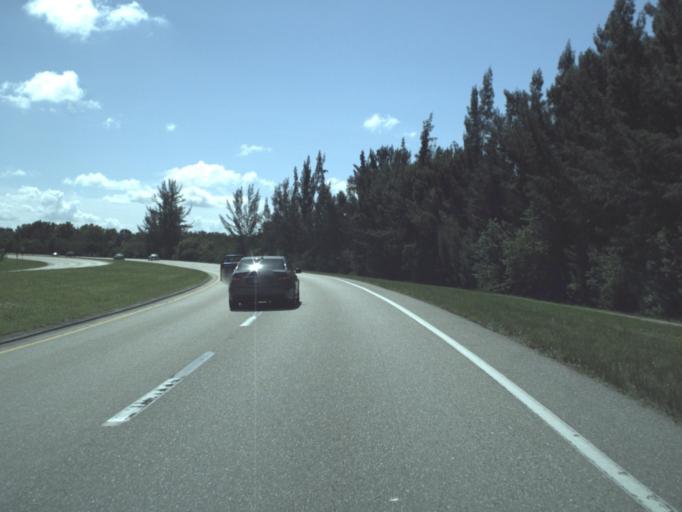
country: US
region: Florida
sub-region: Lee County
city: Pine Island Center
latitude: 26.6102
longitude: -82.0361
